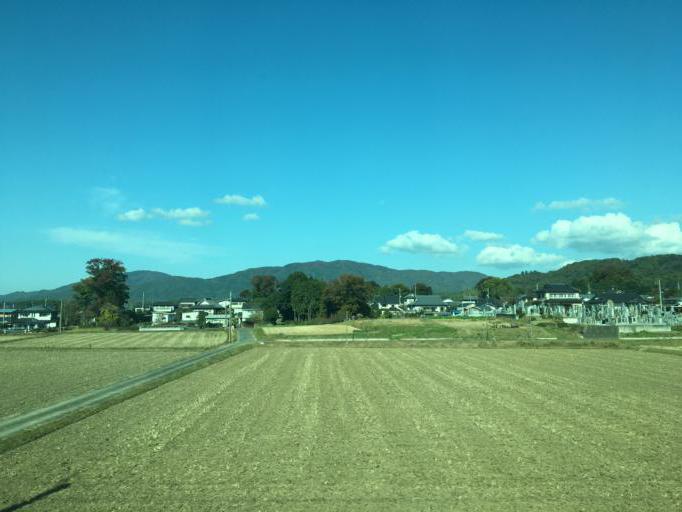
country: JP
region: Ibaraki
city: Iwase
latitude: 36.3539
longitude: 140.1538
